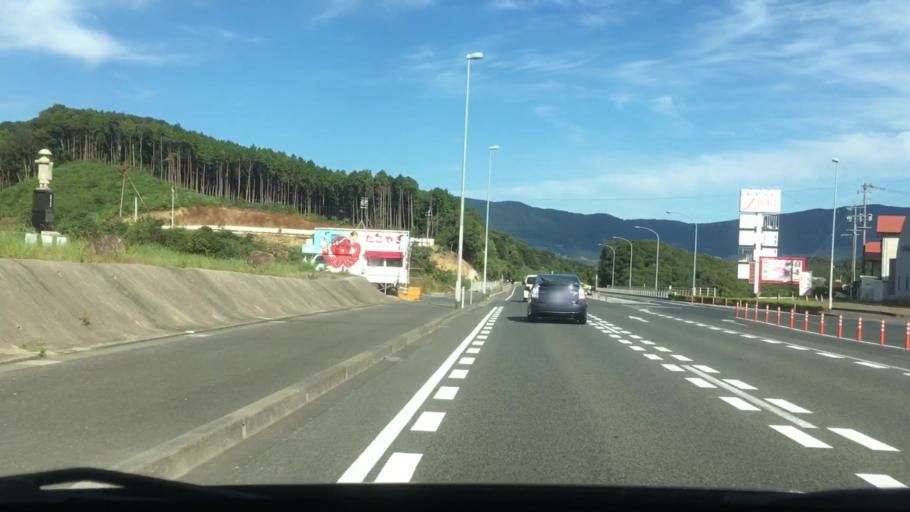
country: JP
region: Nagasaki
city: Sasebo
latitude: 33.1263
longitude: 129.7889
